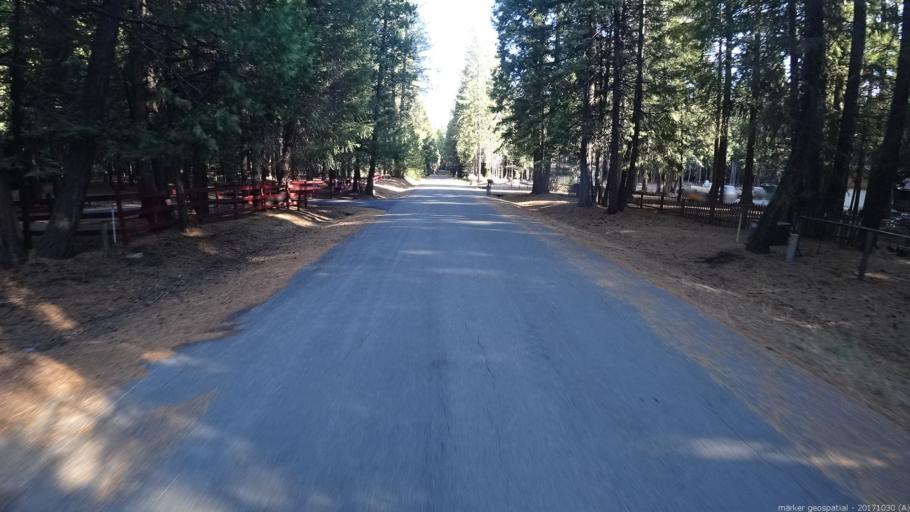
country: US
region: California
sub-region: Shasta County
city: Shingletown
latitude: 40.5534
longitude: -121.7301
